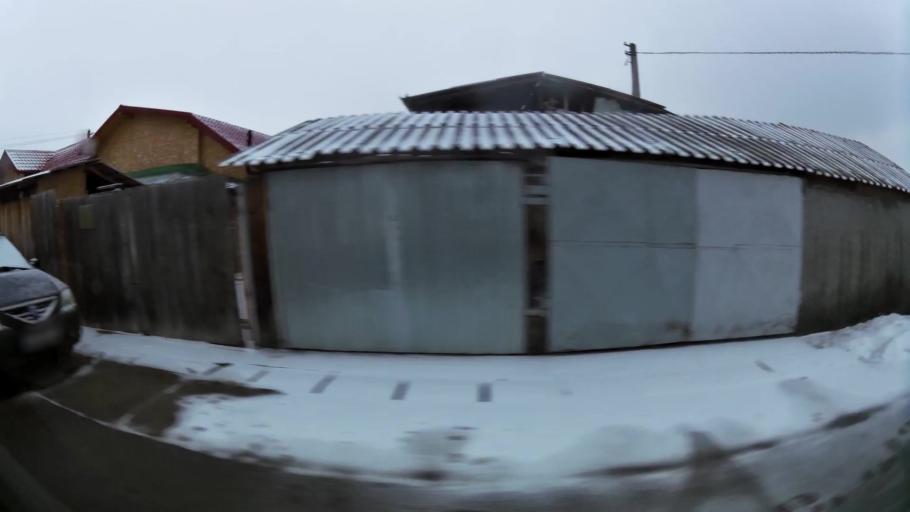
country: RO
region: Prahova
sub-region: Comuna Berceni
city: Corlatesti
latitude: 44.9136
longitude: 26.0909
